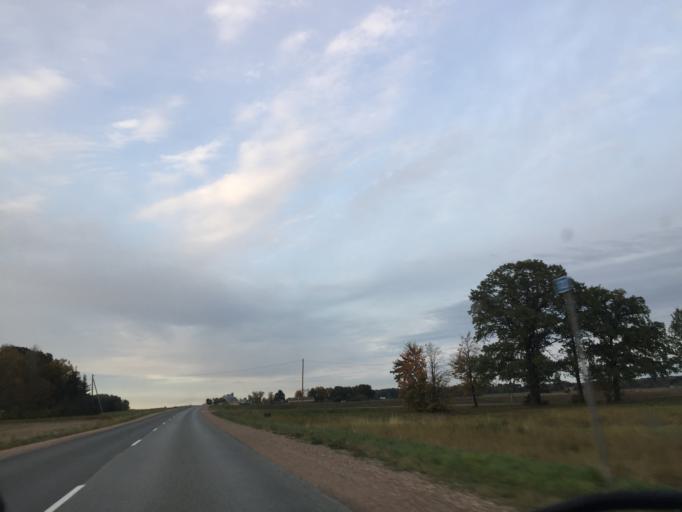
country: LV
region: Dobeles Rajons
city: Dobele
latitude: 56.7125
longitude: 23.3820
